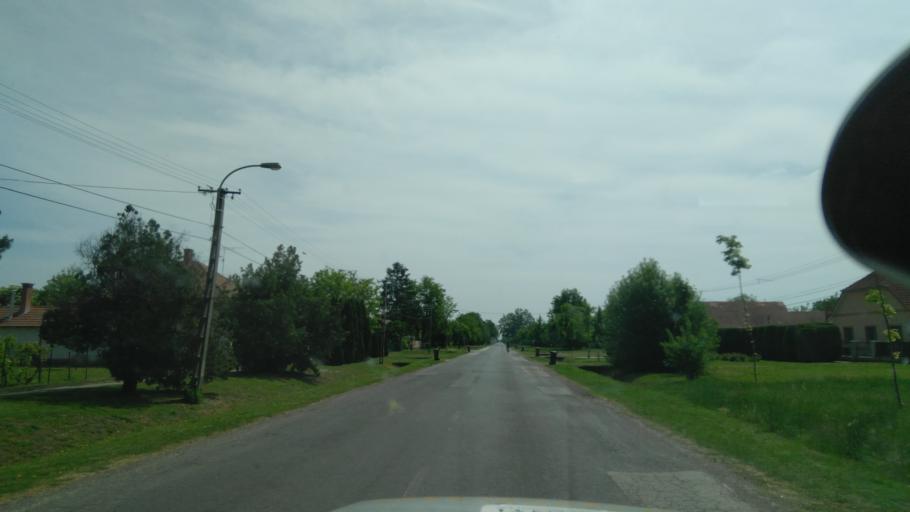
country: HU
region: Csongrad
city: Fabiansebestyen
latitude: 46.5850
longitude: 20.4772
